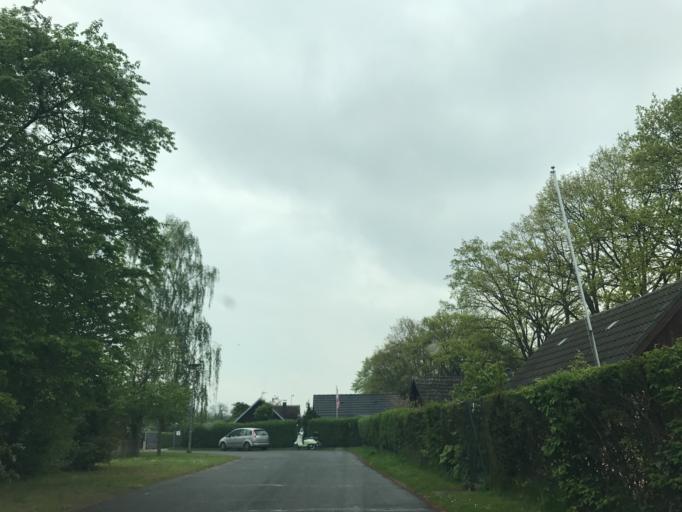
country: DE
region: Berlin
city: Staaken
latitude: 52.5392
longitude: 13.1630
